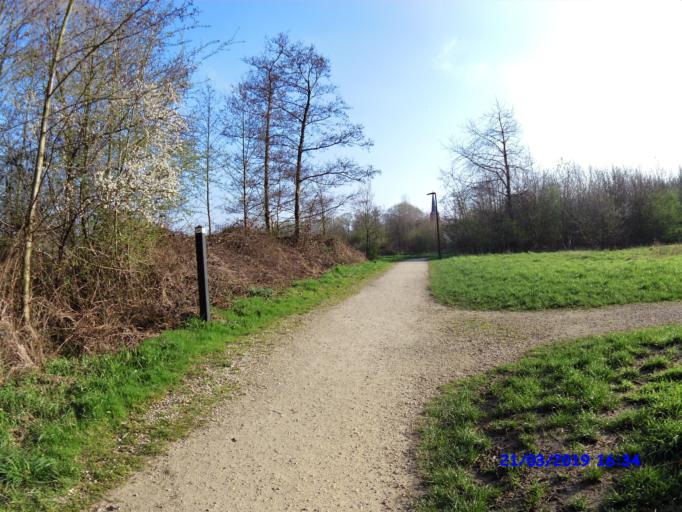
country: BE
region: Flanders
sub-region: Provincie Vlaams-Brabant
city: Beersel
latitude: 50.7499
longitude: 4.2758
